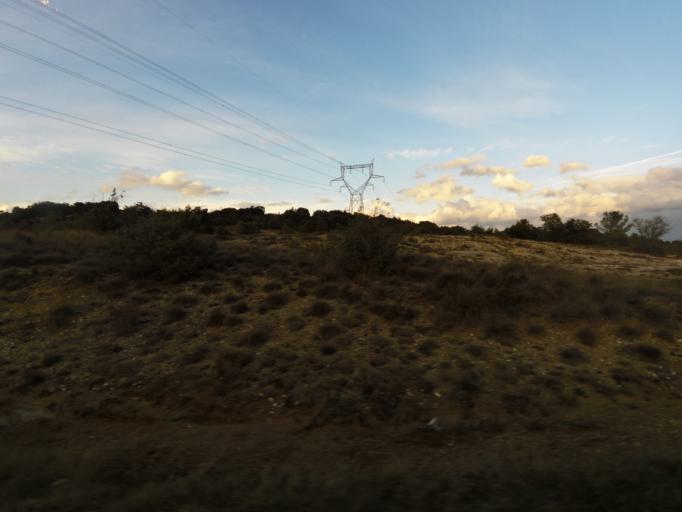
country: FR
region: Languedoc-Roussillon
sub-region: Departement du Gard
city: La Calmette
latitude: 43.8890
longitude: 4.2427
